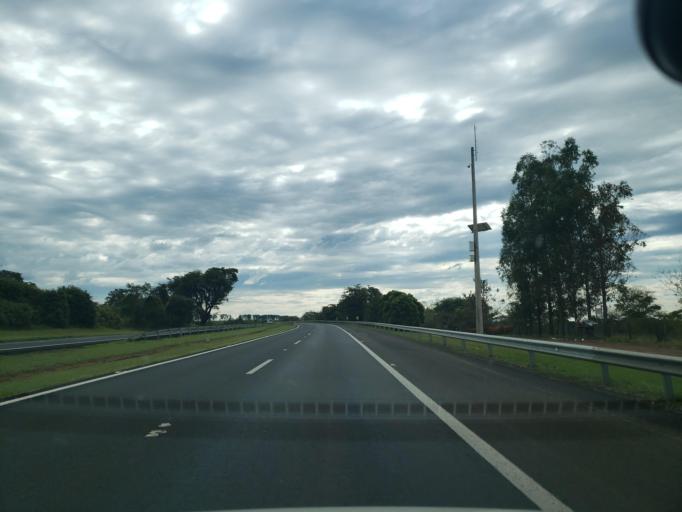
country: BR
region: Sao Paulo
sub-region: Bauru
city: Bauru
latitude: -22.1994
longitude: -49.1870
